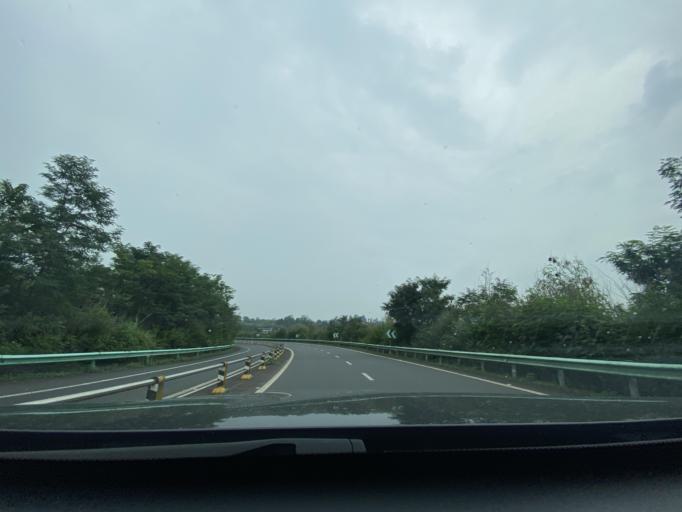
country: CN
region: Sichuan
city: Wenlin
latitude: 30.2957
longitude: 104.1245
